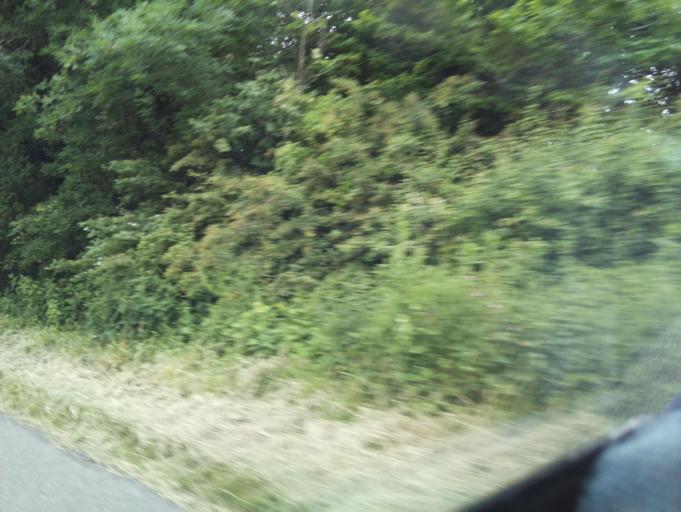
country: GB
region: England
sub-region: Leicestershire
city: Melton Mowbray
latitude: 52.7158
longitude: -0.8297
